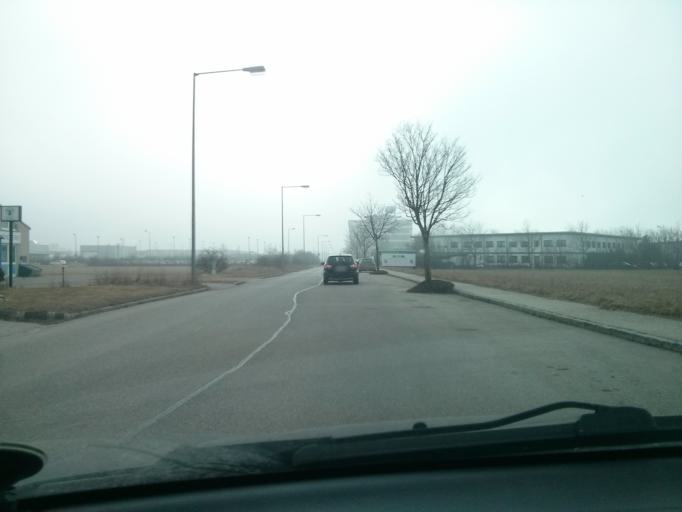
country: AT
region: Lower Austria
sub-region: Politischer Bezirk Wiener Neustadt
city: Theresienfeld
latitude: 47.8418
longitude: 16.2489
